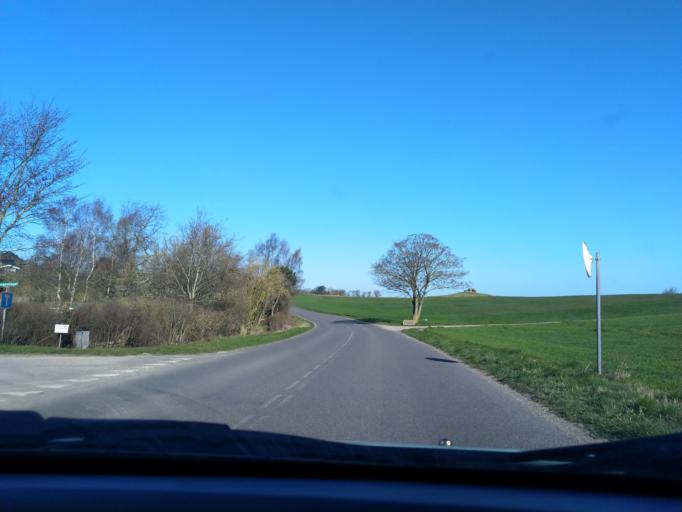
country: DK
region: Zealand
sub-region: Kalundborg Kommune
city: Kalundborg
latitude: 55.7264
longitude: 11.0011
